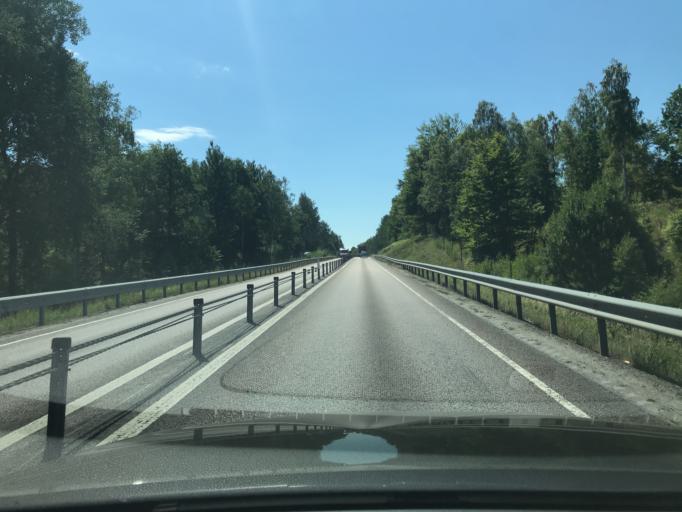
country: SE
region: Kronoberg
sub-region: Vaxjo Kommun
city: Braas
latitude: 56.9898
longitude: 14.9956
